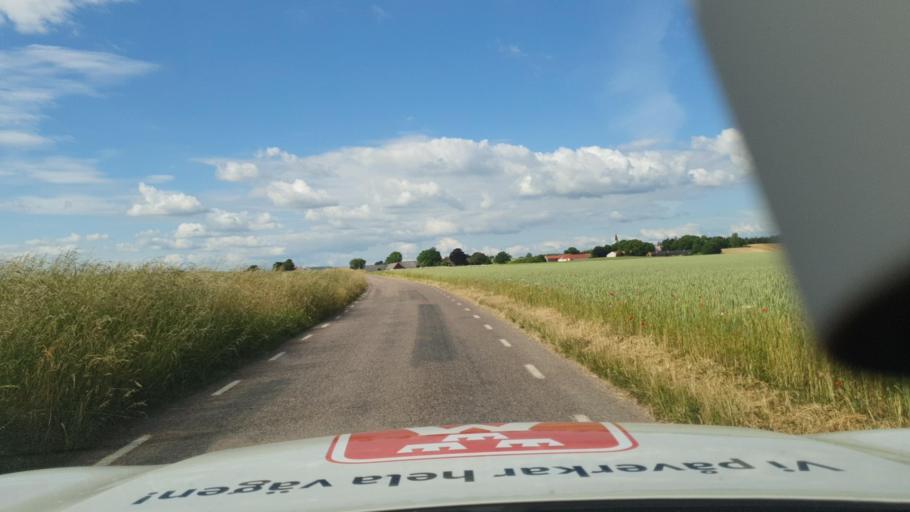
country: SE
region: Skane
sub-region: Skurups Kommun
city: Skurup
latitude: 55.4451
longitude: 13.5189
